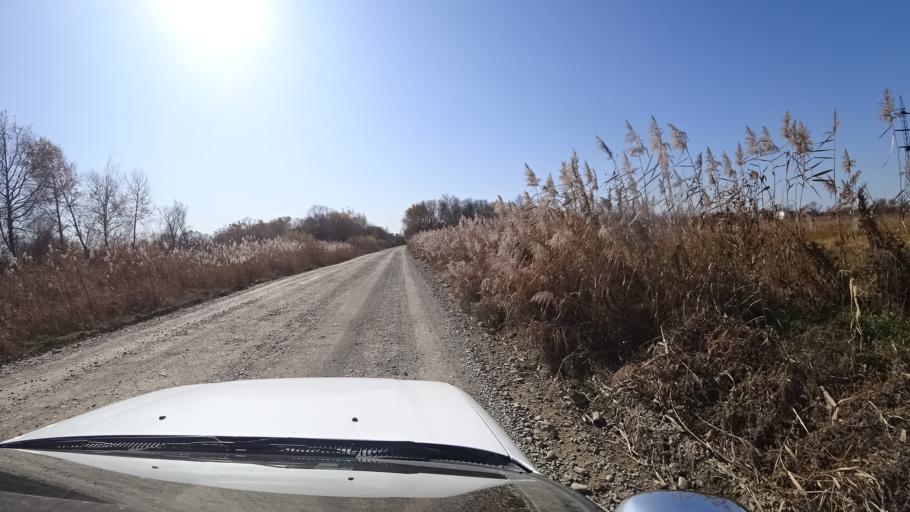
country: RU
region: Primorskiy
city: Dal'nerechensk
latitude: 45.9214
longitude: 133.7780
